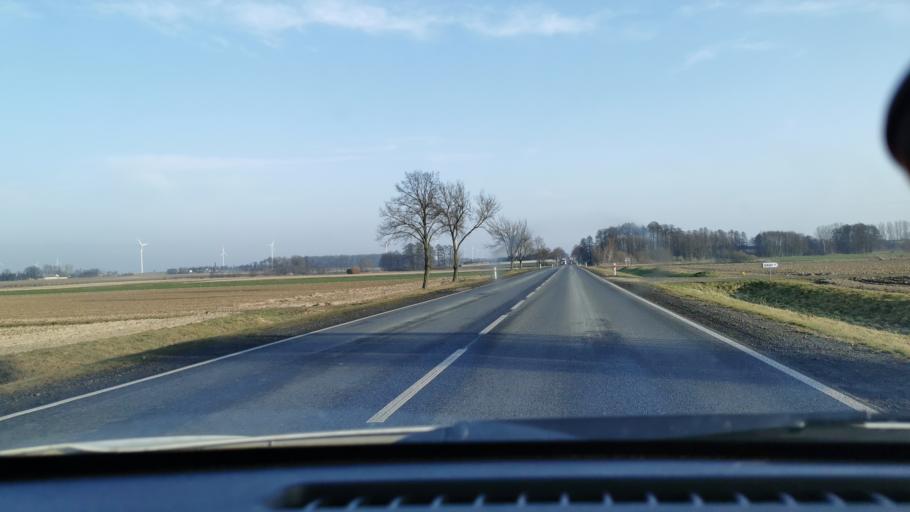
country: PL
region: Lodz Voivodeship
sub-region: Powiat sieradzki
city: Blaszki
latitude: 51.6424
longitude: 18.4907
